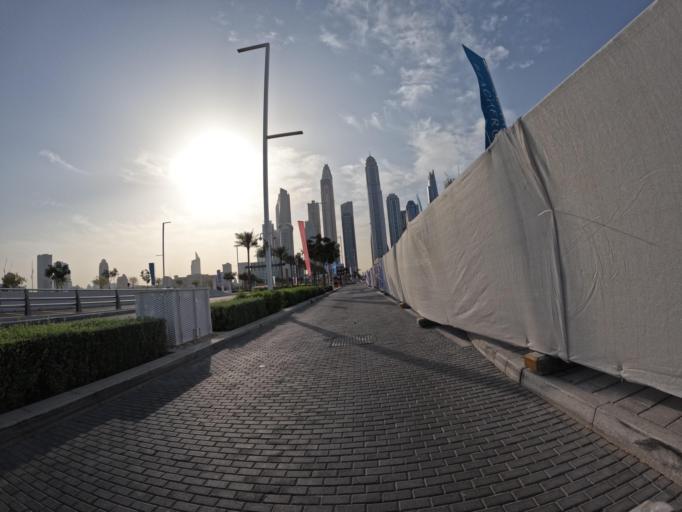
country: AE
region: Dubai
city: Dubai
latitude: 25.0947
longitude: 55.1404
